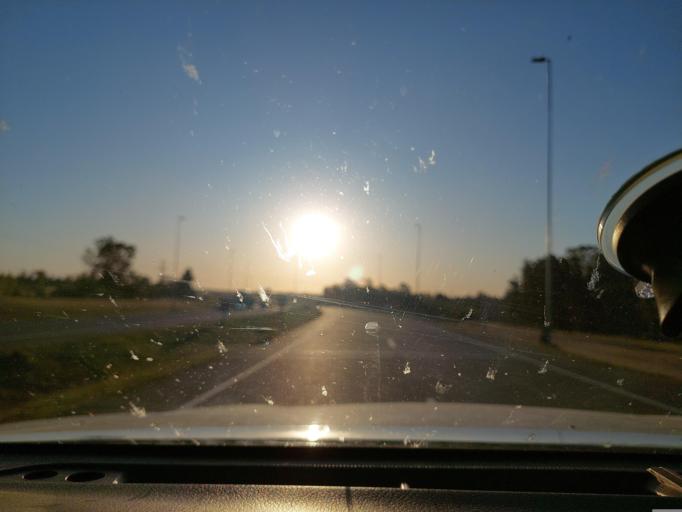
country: UY
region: Canelones
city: Empalme Olmos
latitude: -34.7008
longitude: -55.9181
